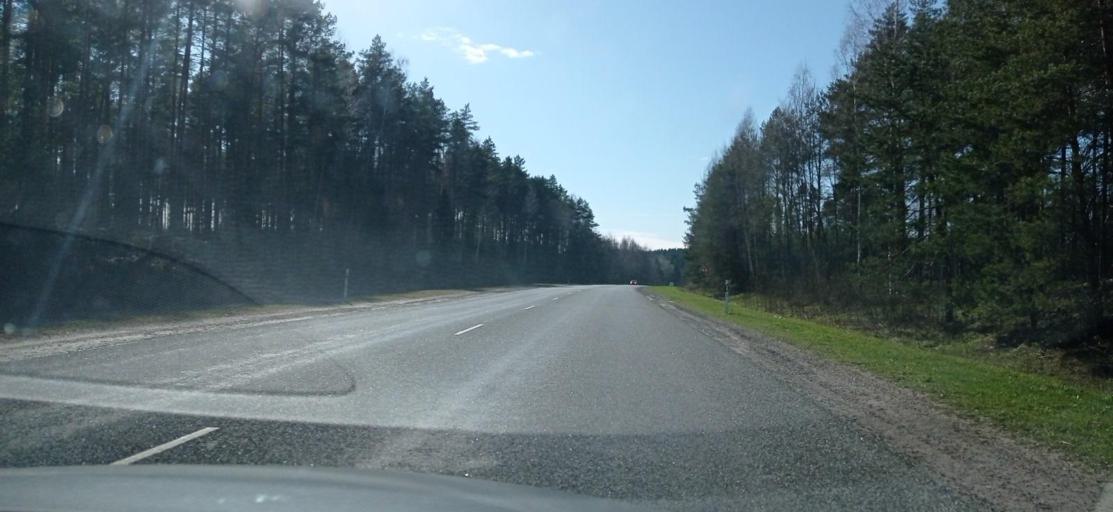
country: LV
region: Valmieras Rajons
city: Valmiera
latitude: 57.5119
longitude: 25.4017
